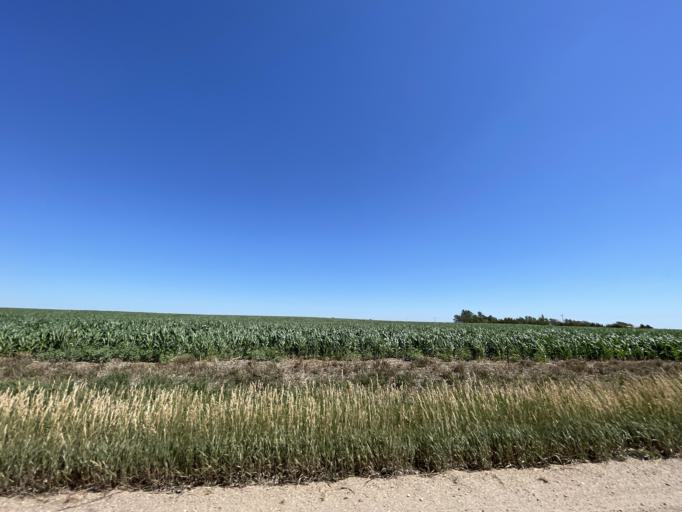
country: US
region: Nebraska
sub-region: Red Willow County
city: McCook
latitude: 40.4373
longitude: -100.6503
